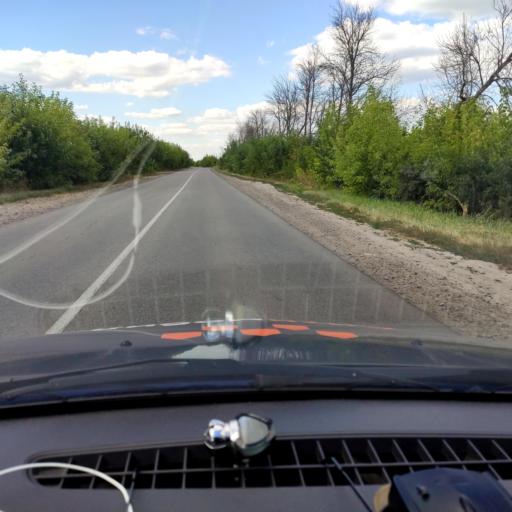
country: RU
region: Voronezj
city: Somovo
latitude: 51.7006
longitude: 39.3739
